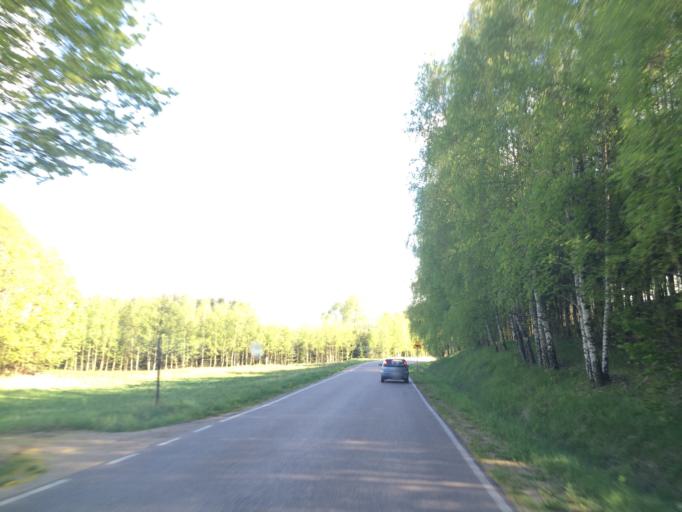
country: PL
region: Warmian-Masurian Voivodeship
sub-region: Powiat dzialdowski
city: Lidzbark
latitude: 53.3044
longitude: 19.8650
